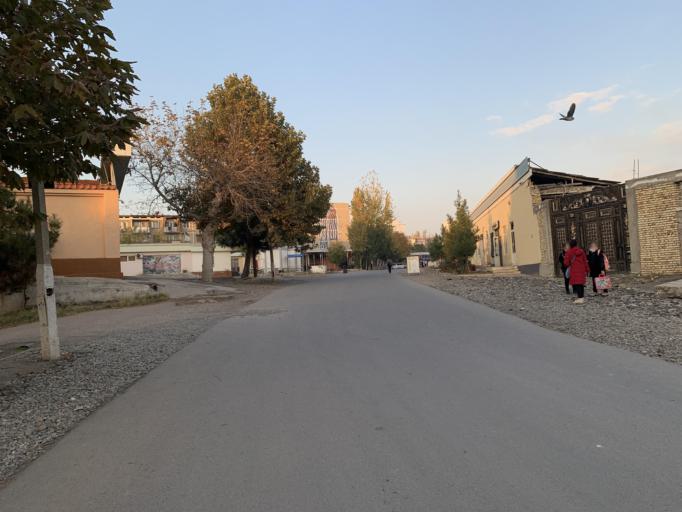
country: UZ
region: Namangan
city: Namangan Shahri
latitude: 41.0044
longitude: 71.5990
